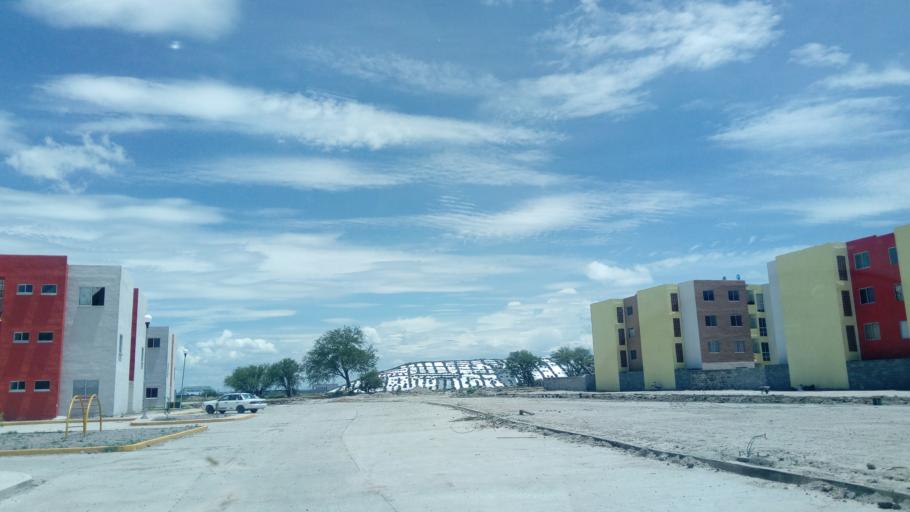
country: MX
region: Durango
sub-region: Durango
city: Jose Refugio Salcido
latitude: 24.0147
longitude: -104.5441
